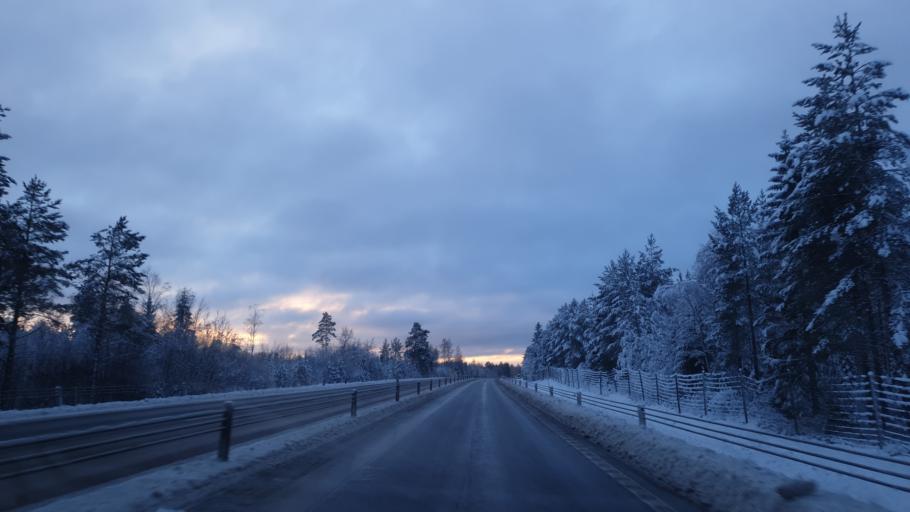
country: SE
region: Vaesterbotten
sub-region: Nordmalings Kommun
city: Nordmaling
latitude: 63.5284
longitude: 19.3915
